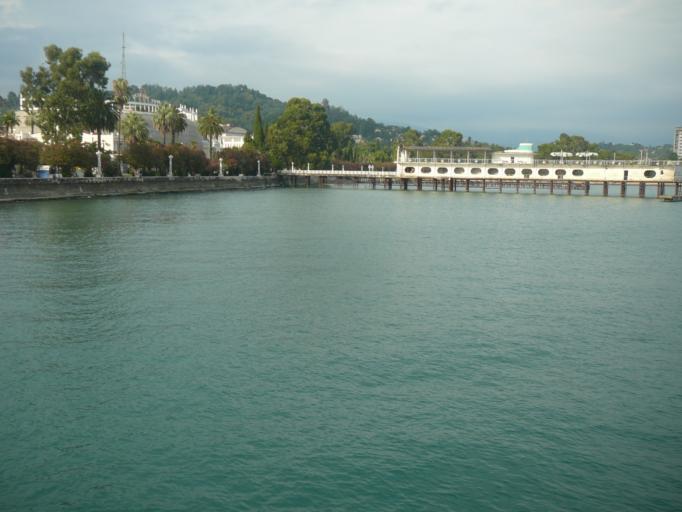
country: GE
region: Abkhazia
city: Sokhumi
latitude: 42.9969
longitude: 41.0225
